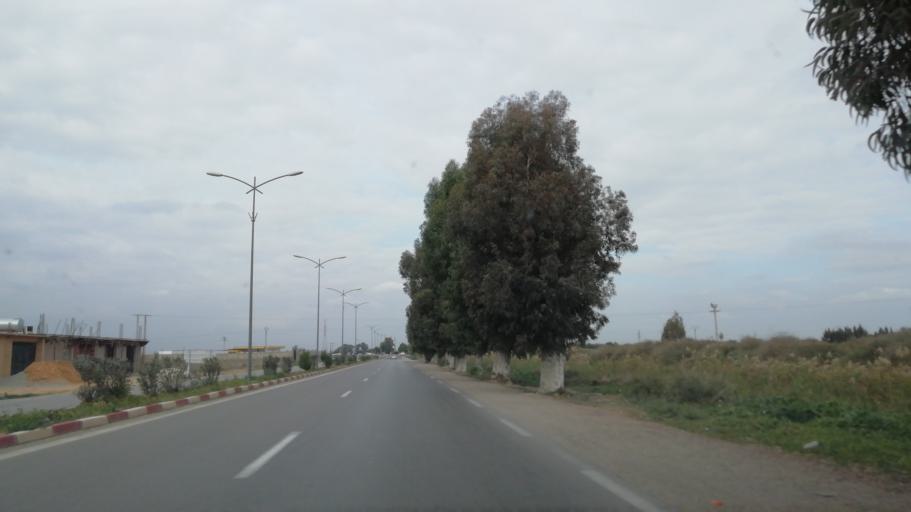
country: DZ
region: Mascara
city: Mascara
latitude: 35.6254
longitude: 0.0617
